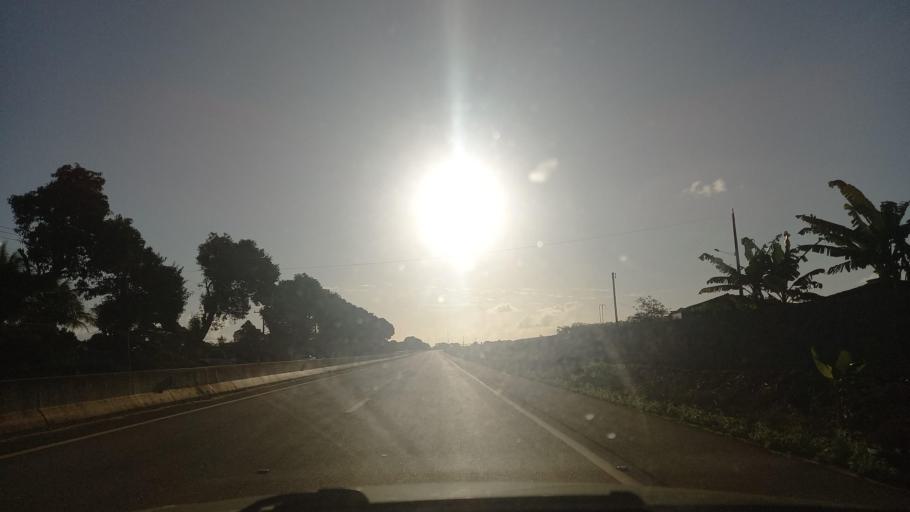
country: BR
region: Alagoas
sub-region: Campo Alegre
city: Campo Alegre
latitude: -9.7898
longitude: -36.3231
